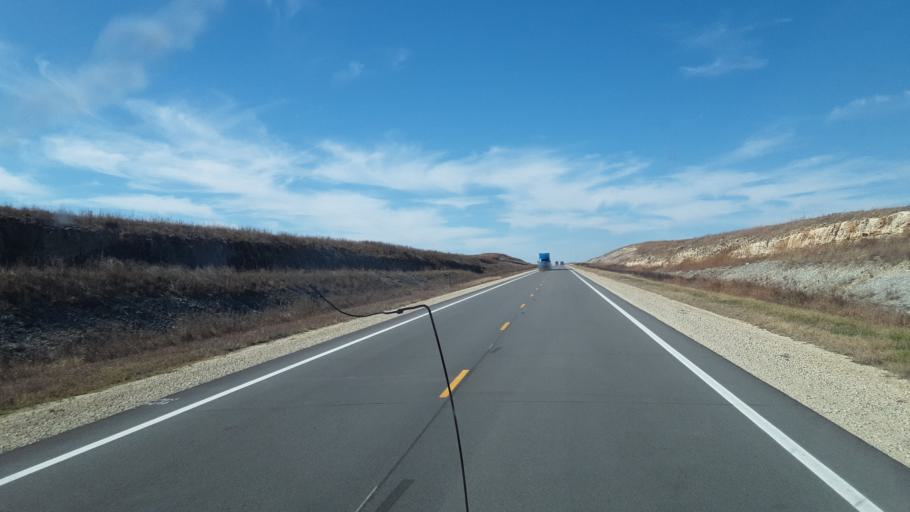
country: US
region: Kansas
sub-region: Chase County
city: Cottonwood Falls
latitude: 38.3627
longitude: -96.6867
